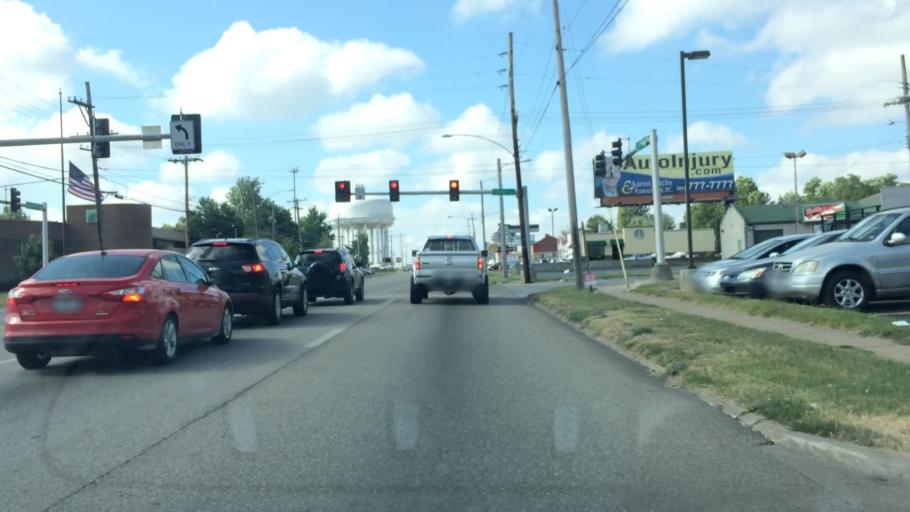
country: US
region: Missouri
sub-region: Greene County
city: Springfield
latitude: 37.2041
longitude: -93.2620
